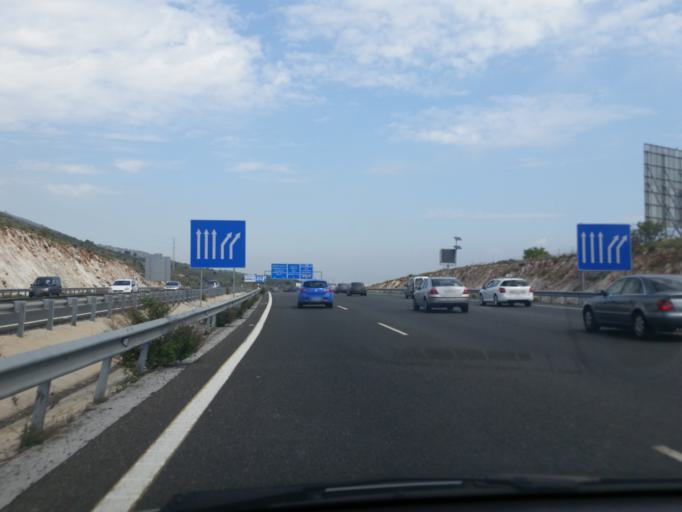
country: ES
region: Andalusia
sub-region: Provincia de Malaga
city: Torremolinos
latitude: 36.6188
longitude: -4.5183
